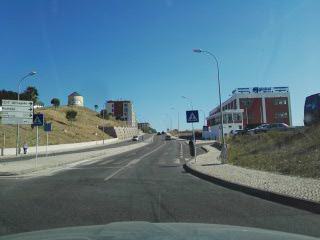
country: PT
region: Lisbon
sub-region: Oeiras
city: Alges
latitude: 38.7184
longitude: -9.2231
